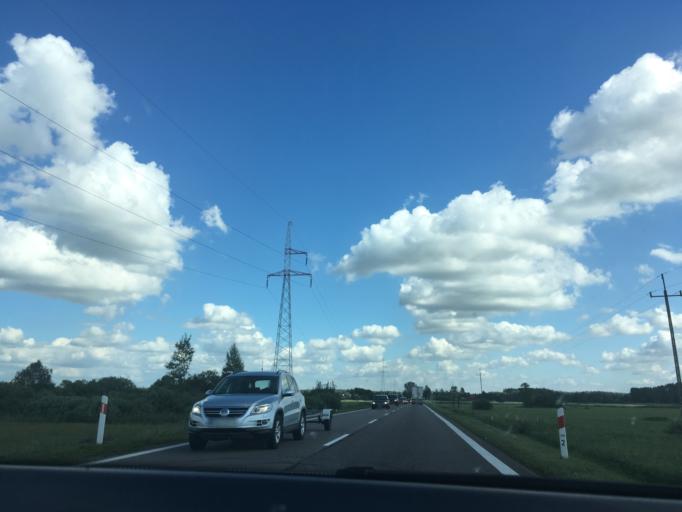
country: PL
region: Podlasie
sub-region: Powiat sokolski
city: Suchowola
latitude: 53.6751
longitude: 23.1094
